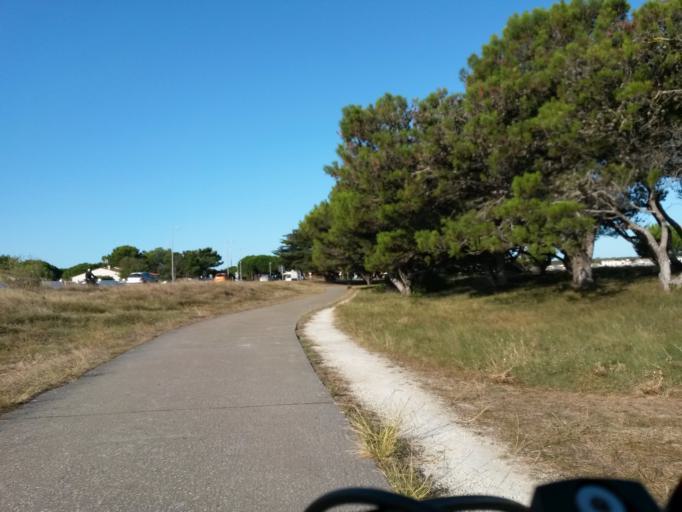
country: FR
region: Poitou-Charentes
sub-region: Departement de la Charente-Maritime
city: Rivedoux-Plage
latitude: 46.1602
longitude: -1.2642
